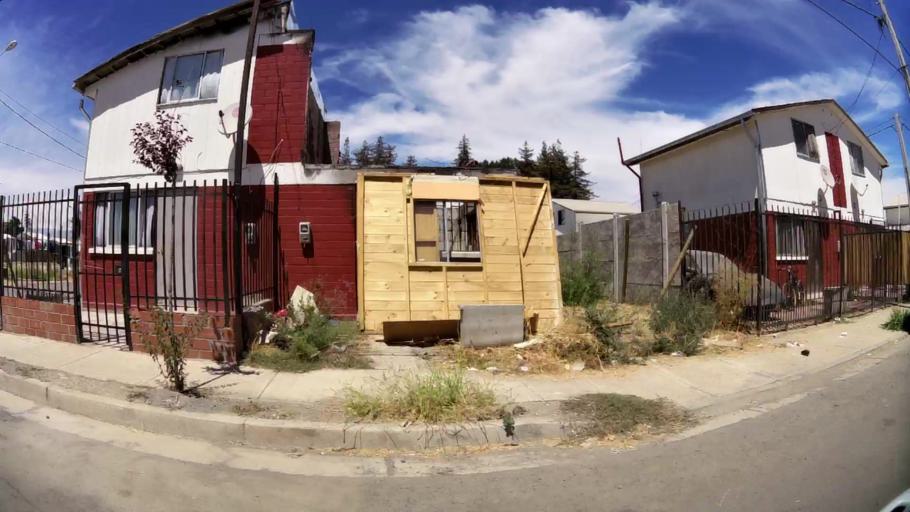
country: CL
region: O'Higgins
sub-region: Provincia de Cachapoal
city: Graneros
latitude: -34.0612
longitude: -70.7217
